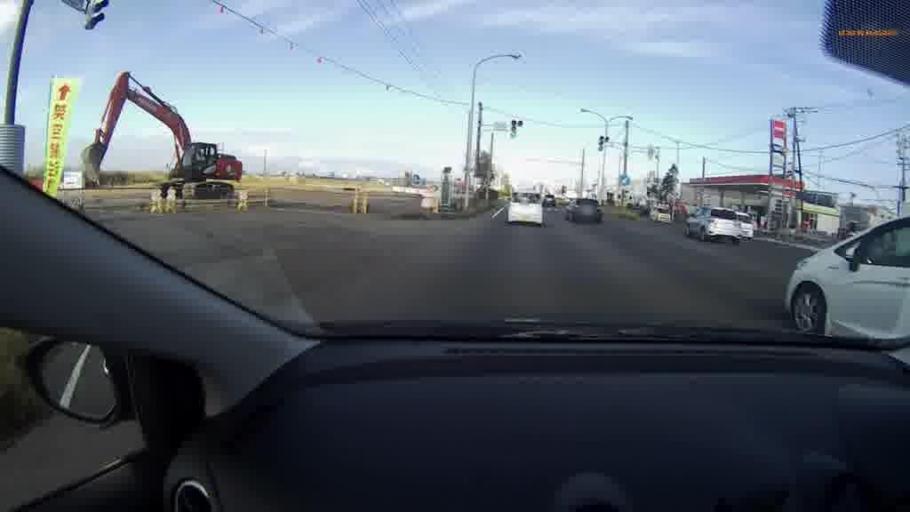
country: JP
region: Hokkaido
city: Kushiro
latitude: 43.0048
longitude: 144.4168
